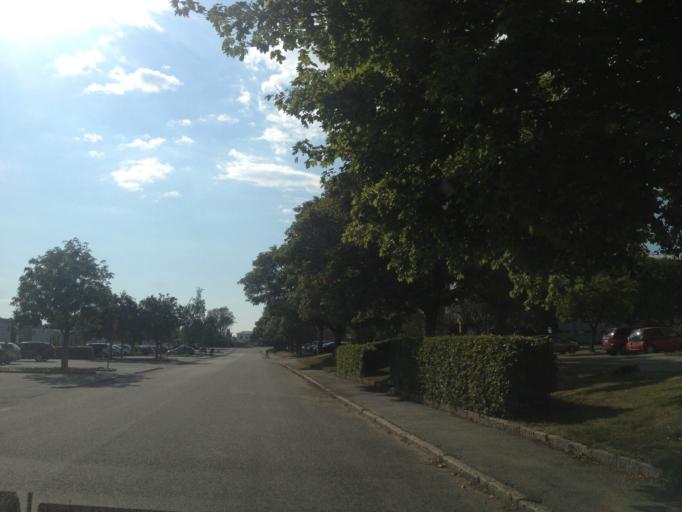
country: SE
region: Vaestra Goetaland
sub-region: Goteborg
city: Majorna
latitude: 57.6710
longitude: 11.9156
